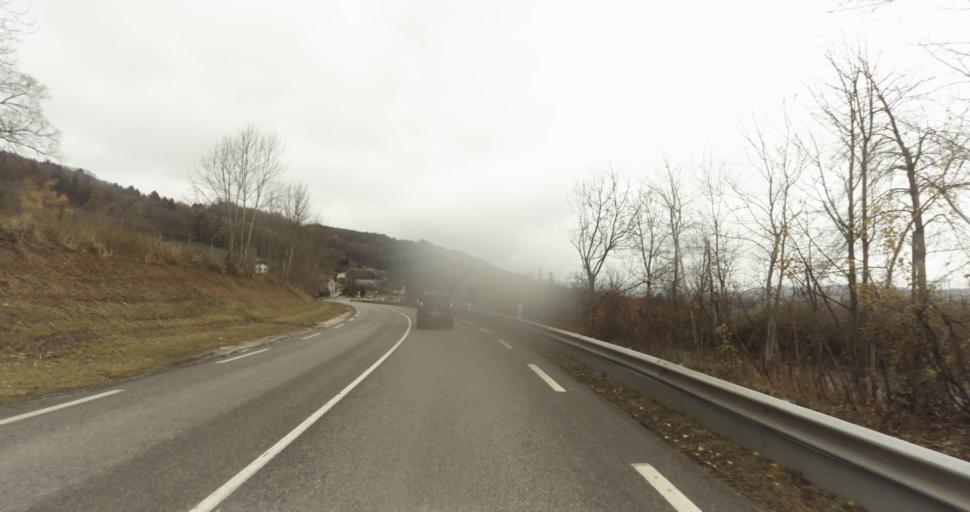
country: FR
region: Rhone-Alpes
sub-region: Departement de la Haute-Savoie
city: Evires
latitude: 46.0242
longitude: 6.2350
